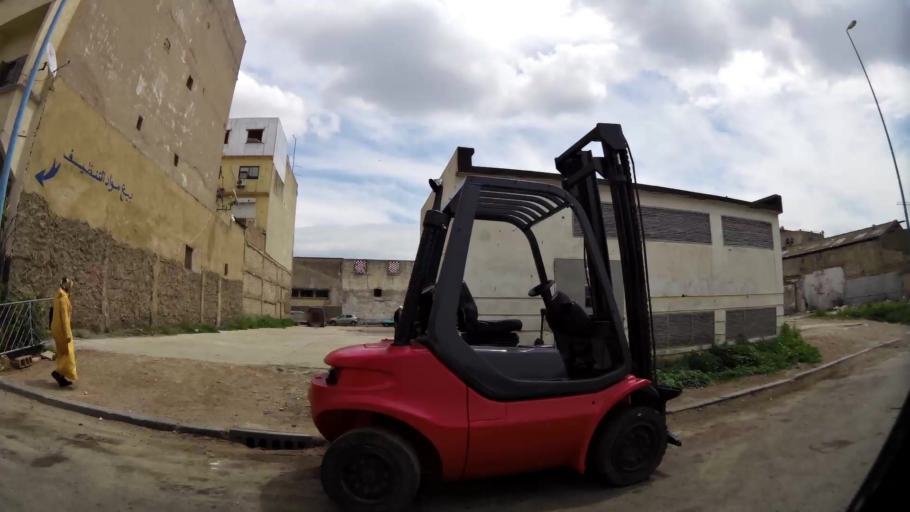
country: MA
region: Grand Casablanca
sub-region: Casablanca
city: Casablanca
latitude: 33.5917
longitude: -7.5781
